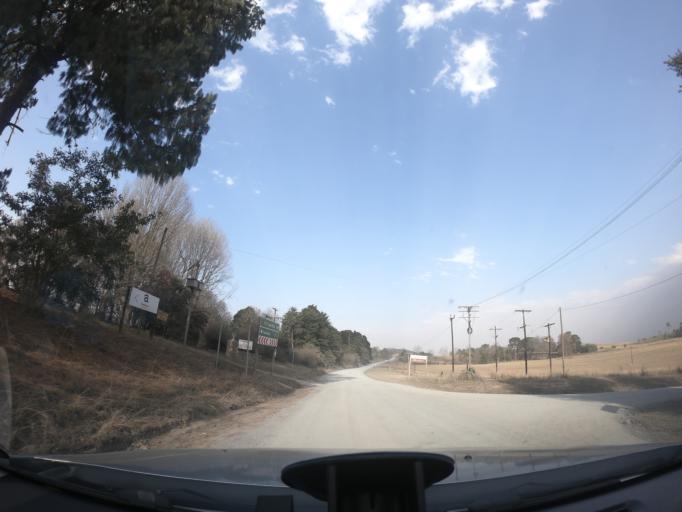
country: ZA
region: KwaZulu-Natal
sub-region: uMgungundlovu District Municipality
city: Howick
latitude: -29.4364
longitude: 30.1149
